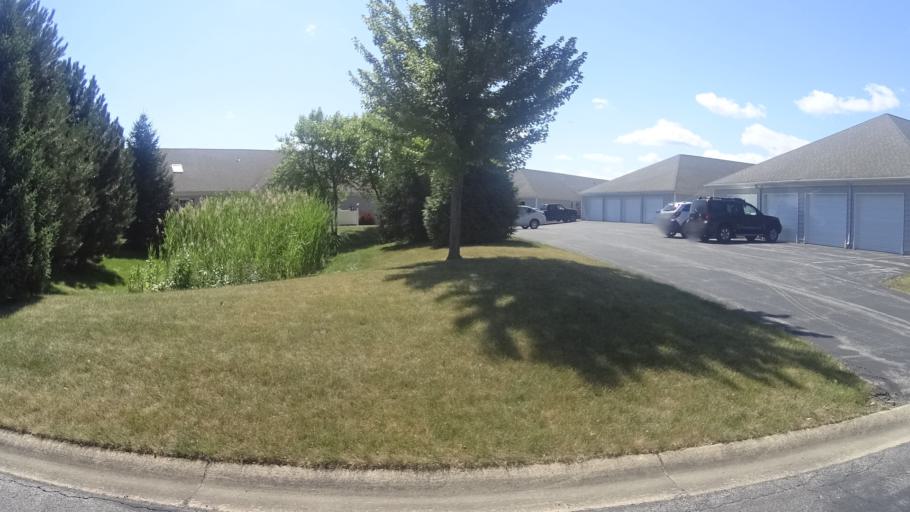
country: US
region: Ohio
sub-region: Erie County
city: Sandusky
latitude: 41.4303
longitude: -82.6606
